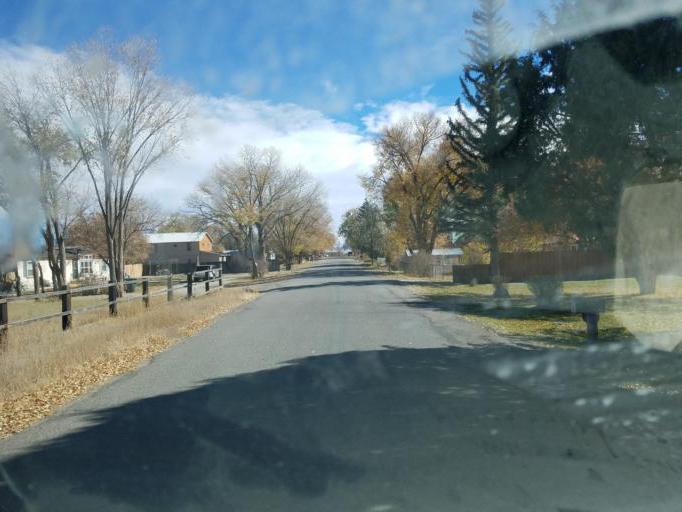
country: US
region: Colorado
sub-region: Alamosa County
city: Alamosa East
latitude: 37.4815
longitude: -105.8545
